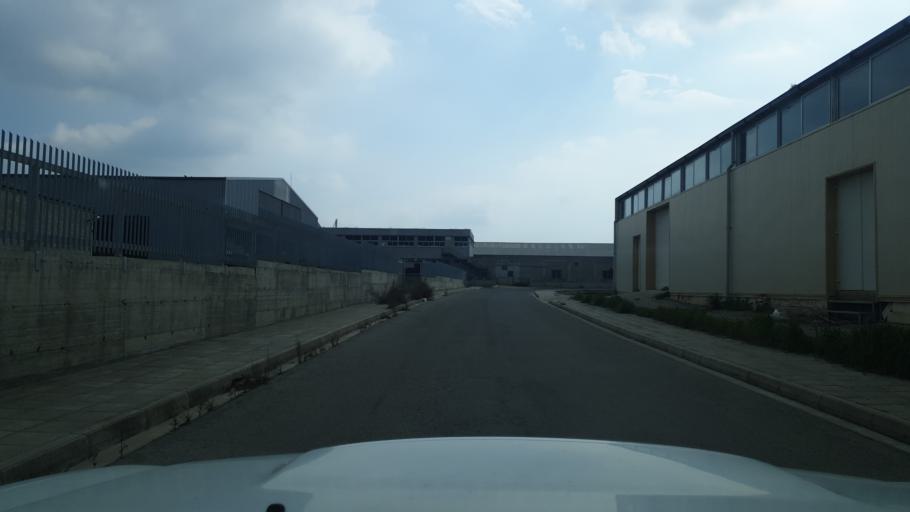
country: CY
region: Lefkosia
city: Geri
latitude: 35.0845
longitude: 33.3872
